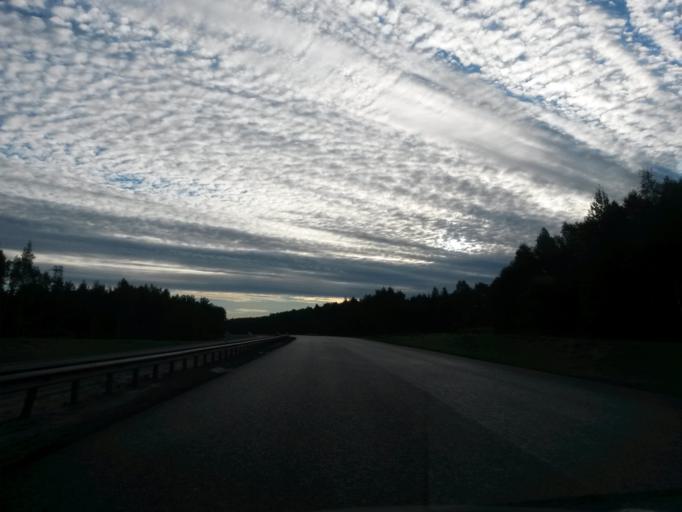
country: RU
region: Vladimir
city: Strunino
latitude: 56.5156
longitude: 38.5486
